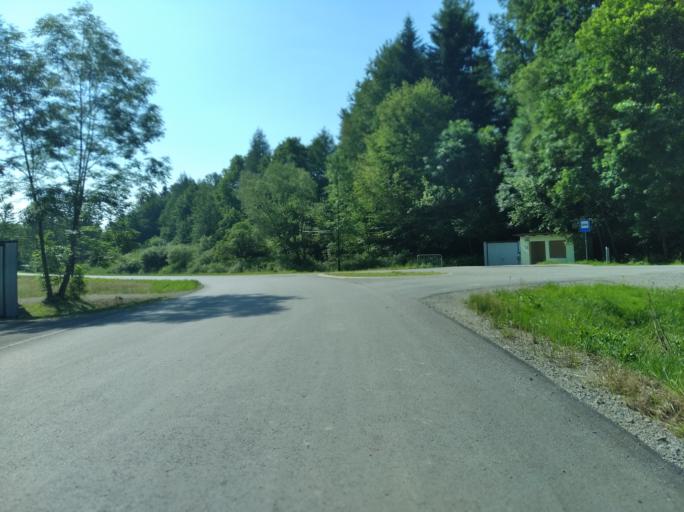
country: PL
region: Subcarpathian Voivodeship
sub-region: Powiat brzozowski
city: Wesola
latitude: 49.8284
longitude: 22.1506
